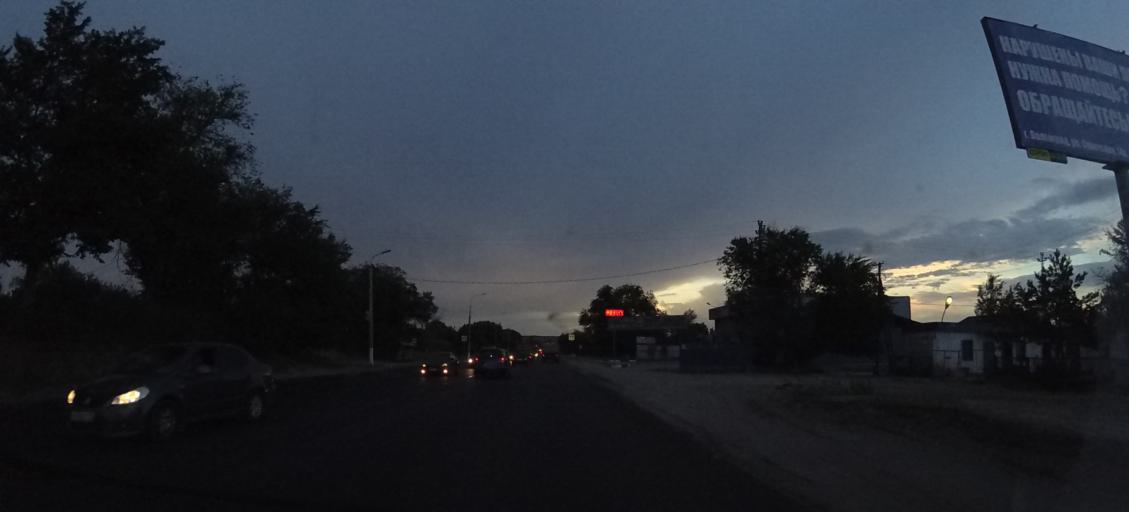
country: RU
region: Volgograd
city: Volgograd
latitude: 48.5728
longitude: 44.4278
